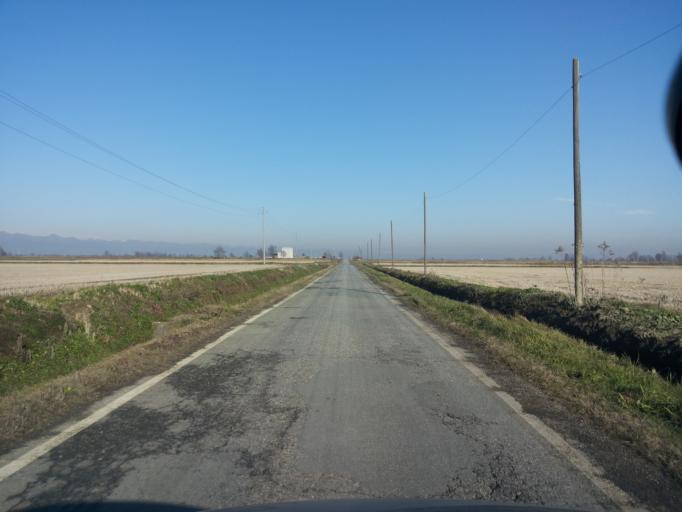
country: IT
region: Piedmont
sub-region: Provincia di Vercelli
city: Formigliana
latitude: 45.4133
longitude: 8.2488
